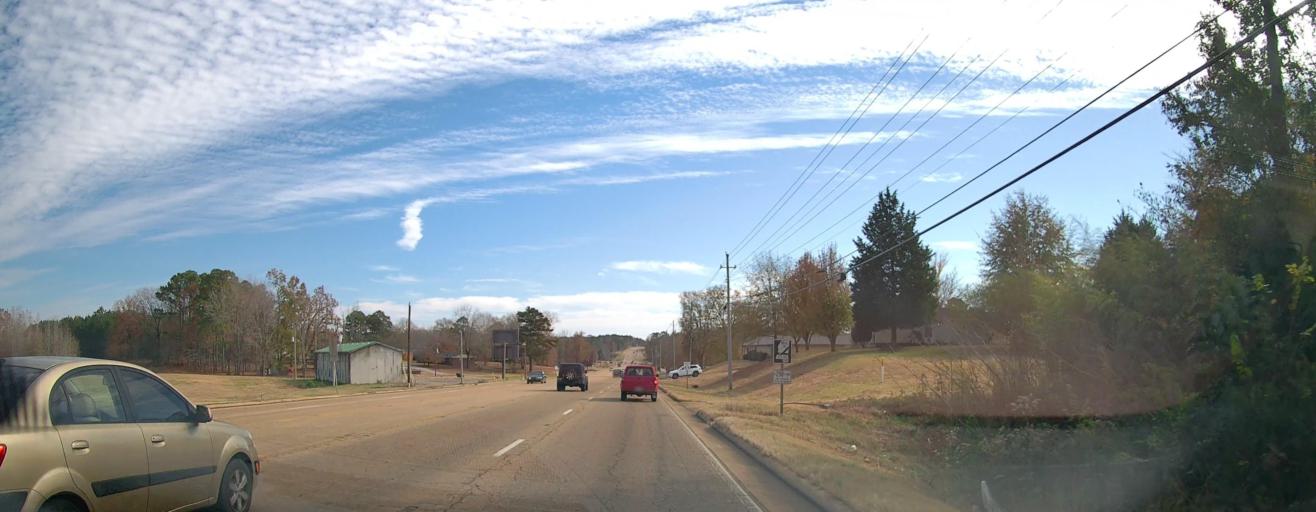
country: US
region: Mississippi
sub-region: Alcorn County
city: Farmington
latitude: 34.9047
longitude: -88.4843
